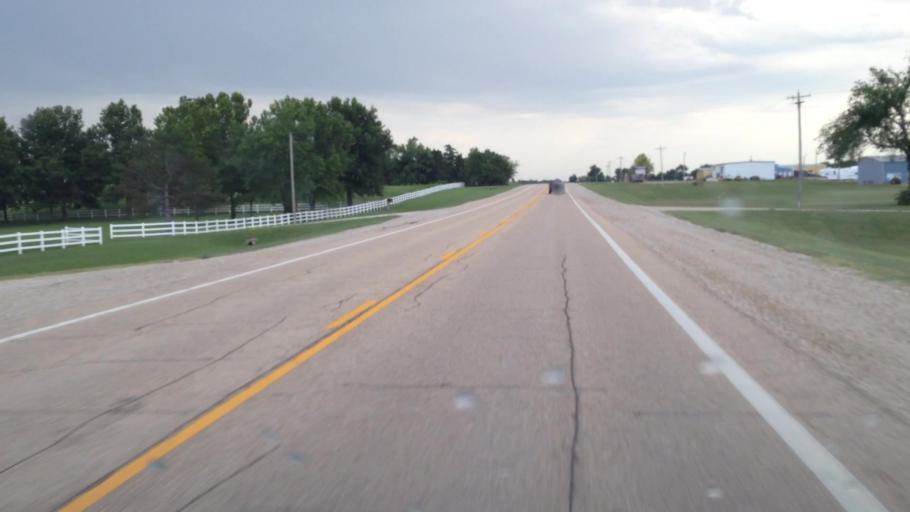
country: US
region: Kansas
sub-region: Coffey County
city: Burlington
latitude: 38.1813
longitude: -95.7388
